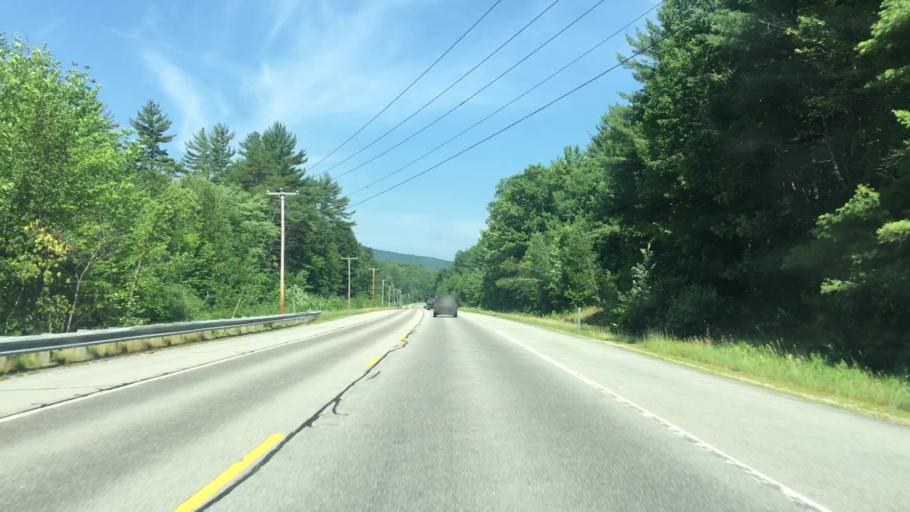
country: US
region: New Hampshire
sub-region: Merrimack County
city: Newbury
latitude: 43.2999
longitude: -72.0018
